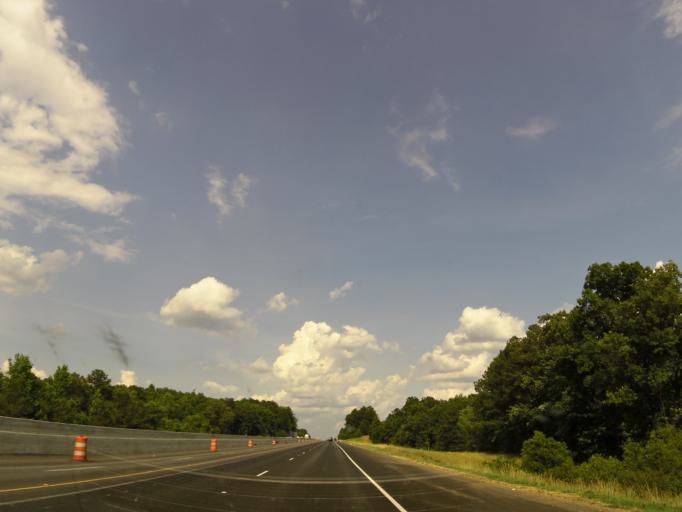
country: US
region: Alabama
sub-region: Tuscaloosa County
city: Coaling
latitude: 33.1762
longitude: -87.3929
